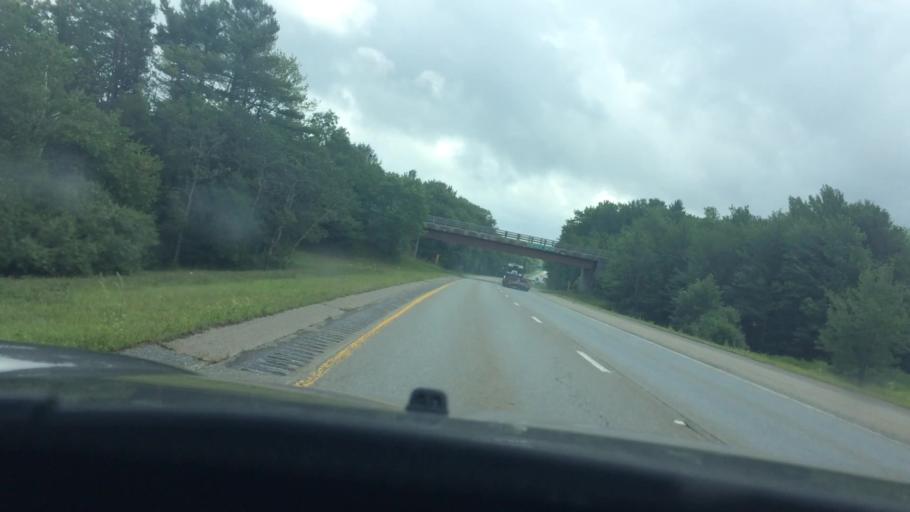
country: US
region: Massachusetts
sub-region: Worcester County
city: Templeton
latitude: 42.5653
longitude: -72.0596
